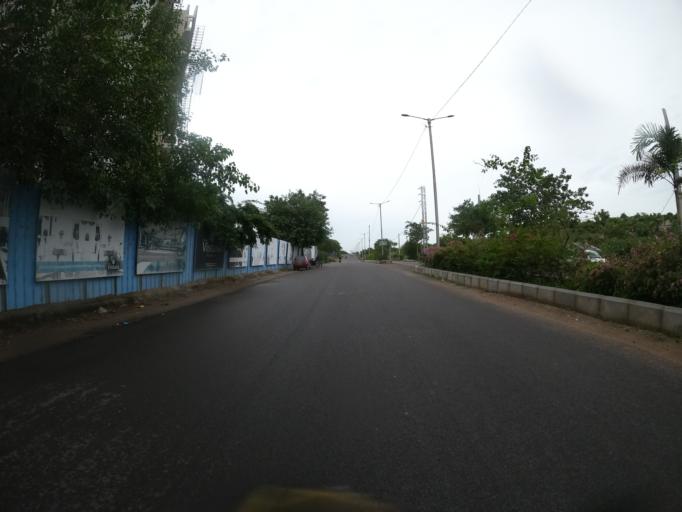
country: IN
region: Telangana
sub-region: Rangareddi
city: Kukatpalli
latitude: 17.4612
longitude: 78.3915
